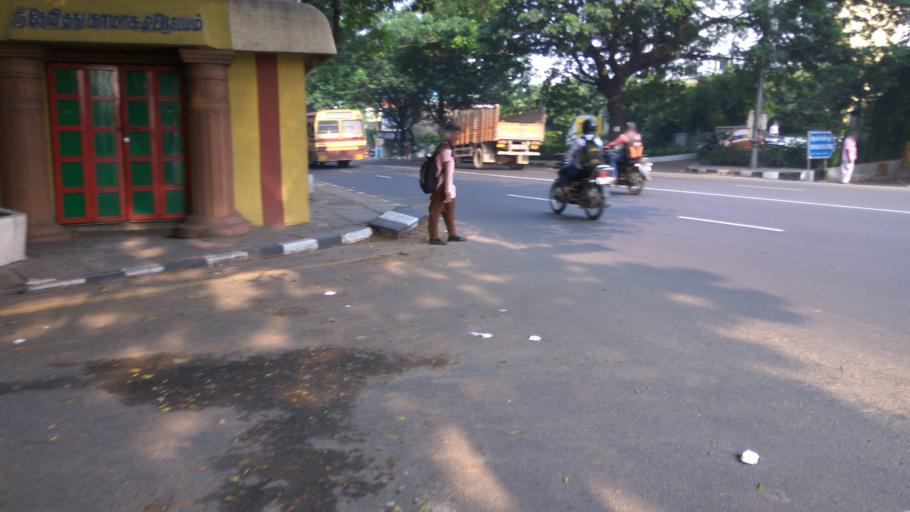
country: IN
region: Tamil Nadu
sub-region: Kancheepuram
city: Alandur
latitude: 13.0106
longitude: 80.2249
